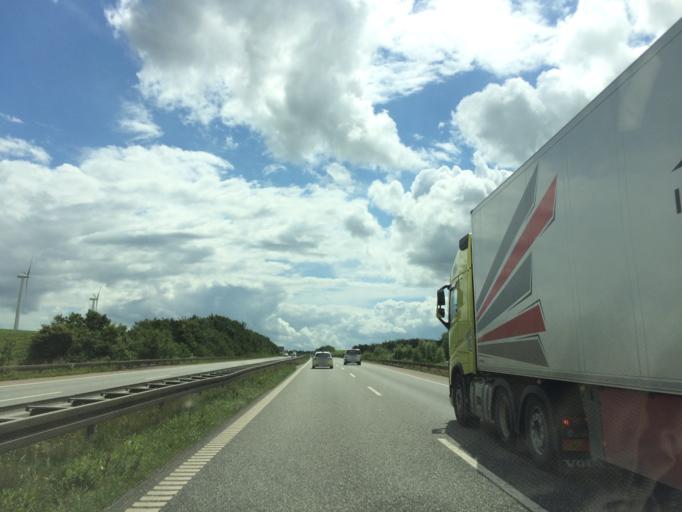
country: DK
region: North Denmark
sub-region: Mariagerfjord Kommune
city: Hobro
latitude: 56.7668
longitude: 9.6936
